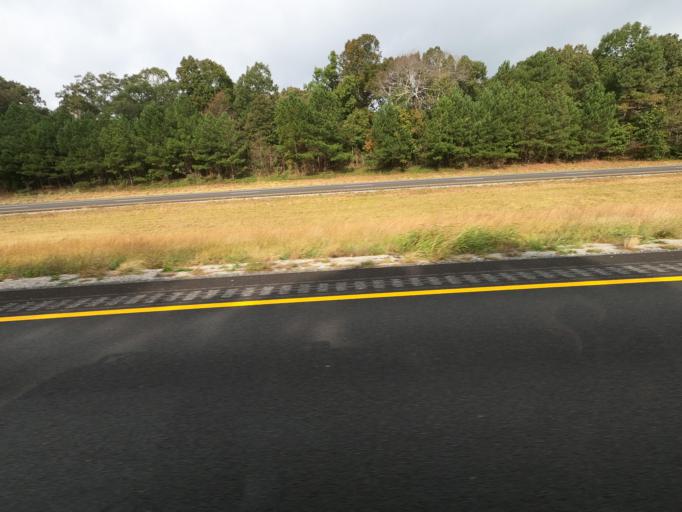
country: US
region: Tennessee
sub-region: Humphreys County
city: McEwen
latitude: 35.9618
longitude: -87.5480
